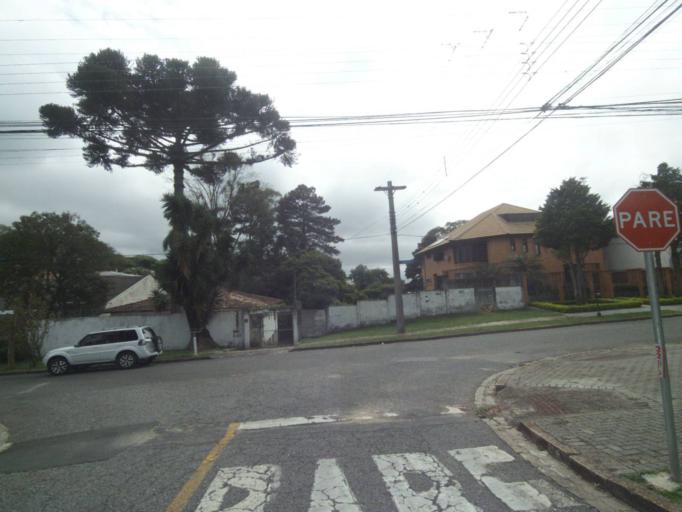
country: BR
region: Parana
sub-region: Curitiba
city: Curitiba
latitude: -25.4265
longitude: -49.2401
